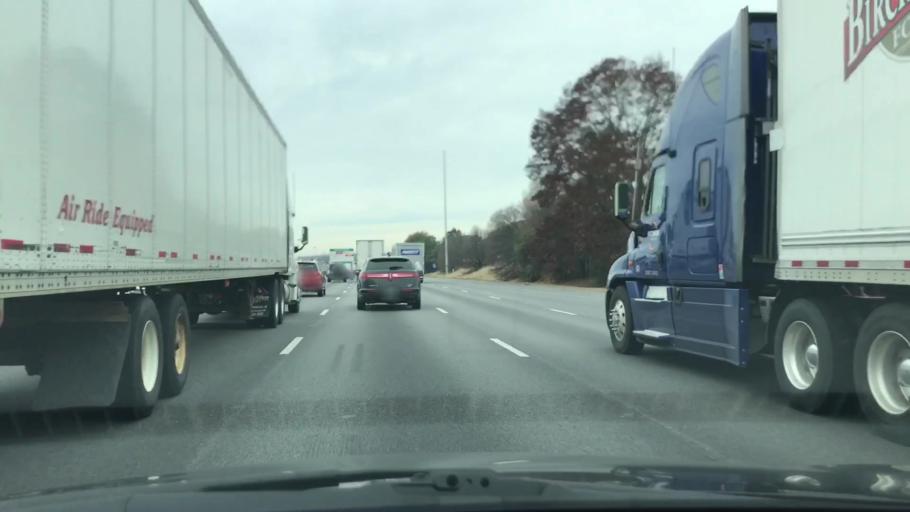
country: US
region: Georgia
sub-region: Gwinnett County
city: Norcross
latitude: 33.9111
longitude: -84.2160
